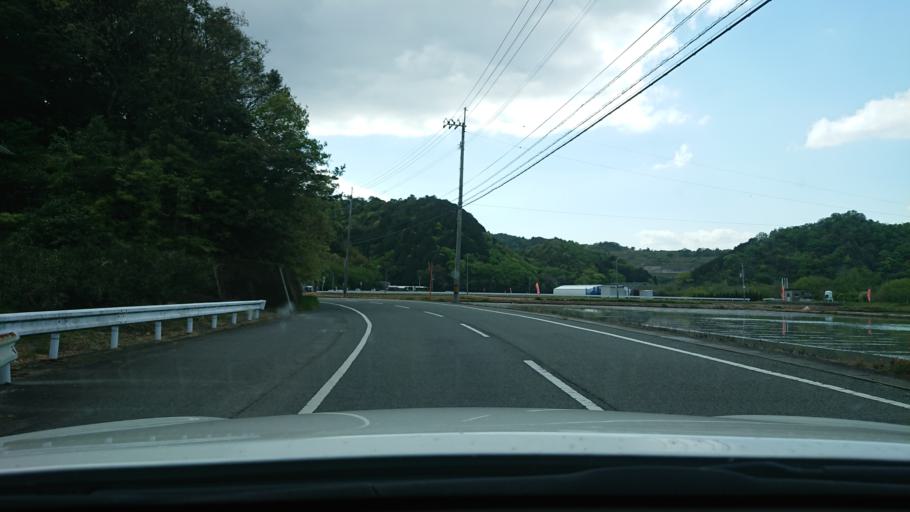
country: JP
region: Tokushima
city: Komatsushimacho
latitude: 33.9814
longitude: 134.5493
